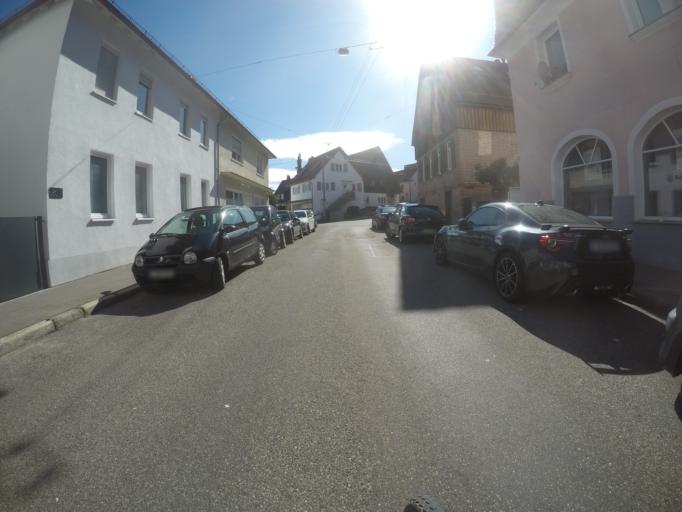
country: DE
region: Baden-Wuerttemberg
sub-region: Regierungsbezirk Stuttgart
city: Stuttgart
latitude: 48.7470
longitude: 9.1732
